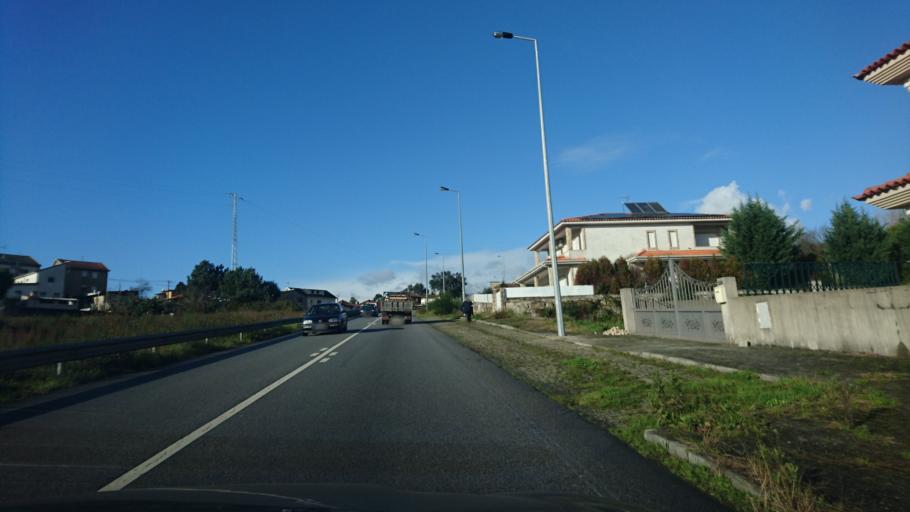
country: PT
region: Porto
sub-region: Paredes
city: Recarei
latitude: 41.1516
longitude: -8.4008
